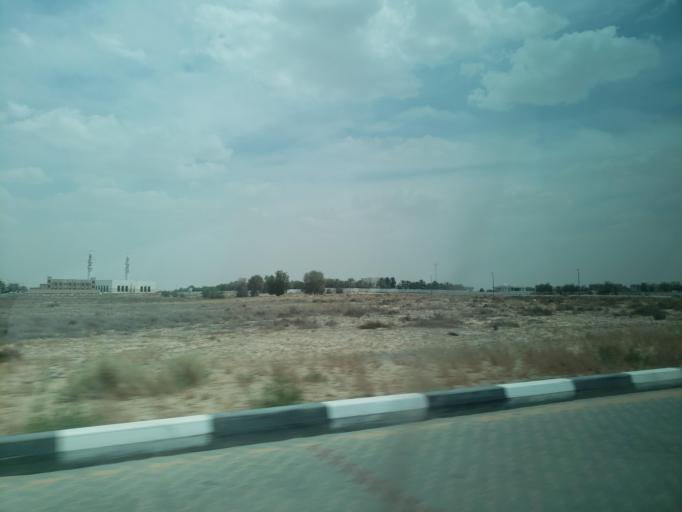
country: AE
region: Ash Shariqah
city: Sharjah
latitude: 25.3176
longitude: 55.5084
